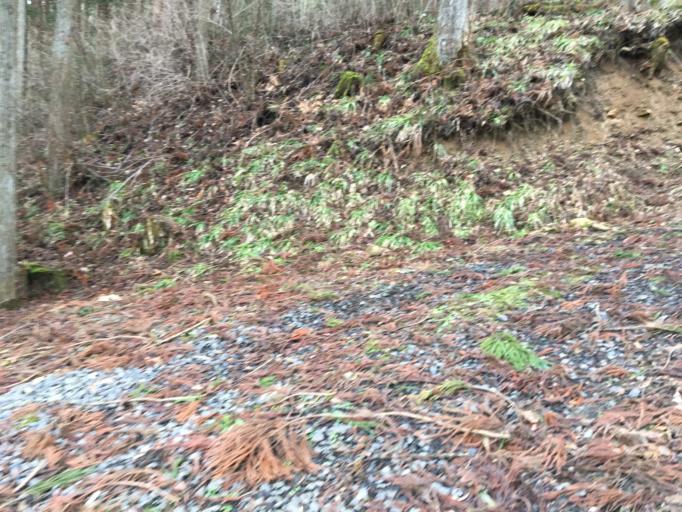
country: JP
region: Iwate
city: Ichinoseki
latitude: 38.9852
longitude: 141.2104
